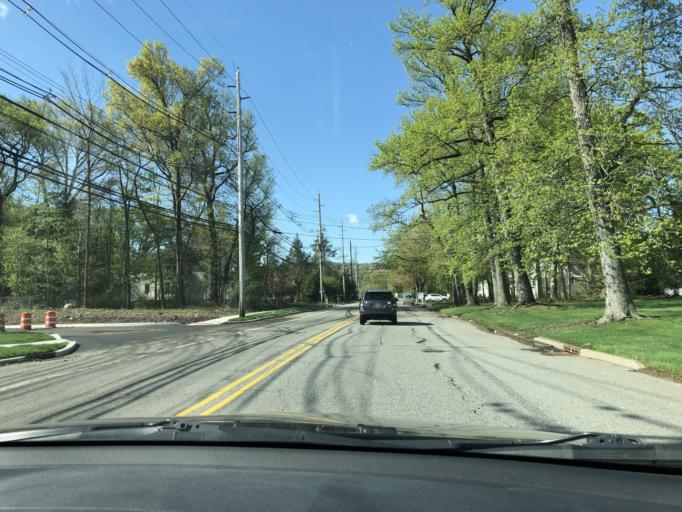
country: US
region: New Jersey
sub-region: Passaic County
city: Singac
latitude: 40.8873
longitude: -74.2306
